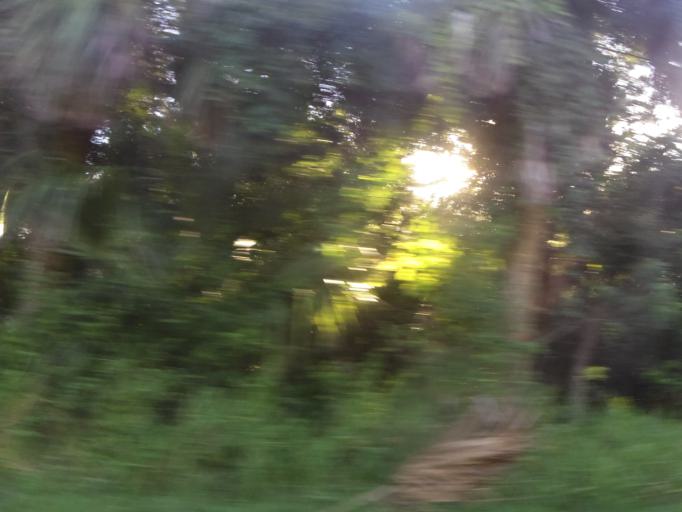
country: US
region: Florida
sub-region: Flagler County
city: Flagler Beach
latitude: 29.4575
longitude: -81.1199
